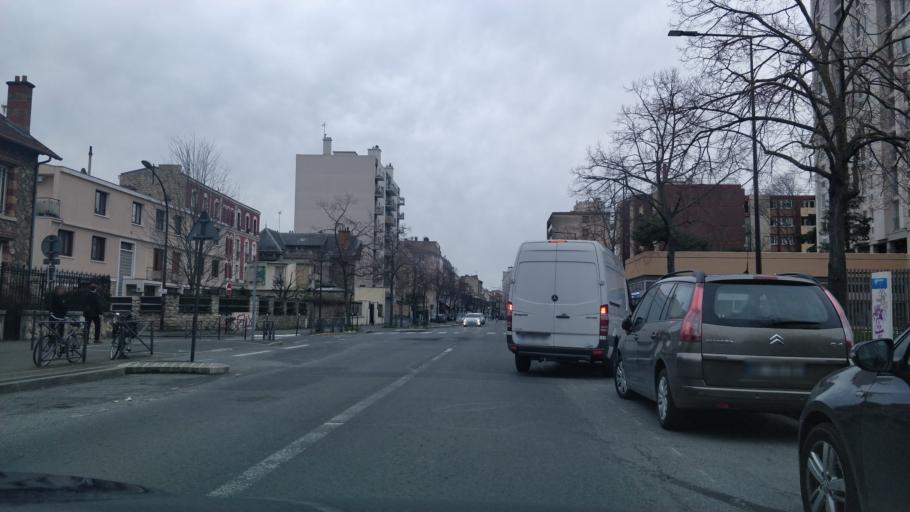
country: FR
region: Ile-de-France
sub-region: Departement du Val-de-Marne
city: Ivry-sur-Seine
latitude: 48.8144
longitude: 2.3843
